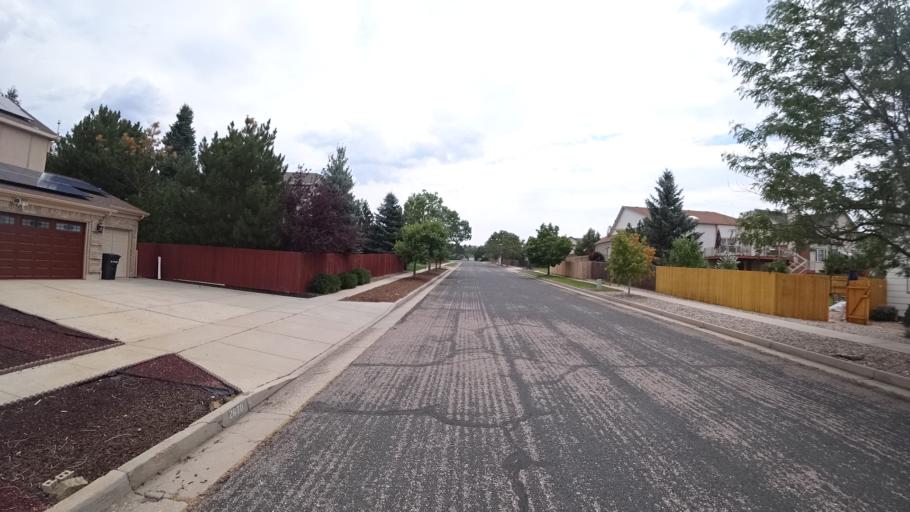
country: US
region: Colorado
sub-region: El Paso County
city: Black Forest
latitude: 38.9601
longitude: -104.7729
